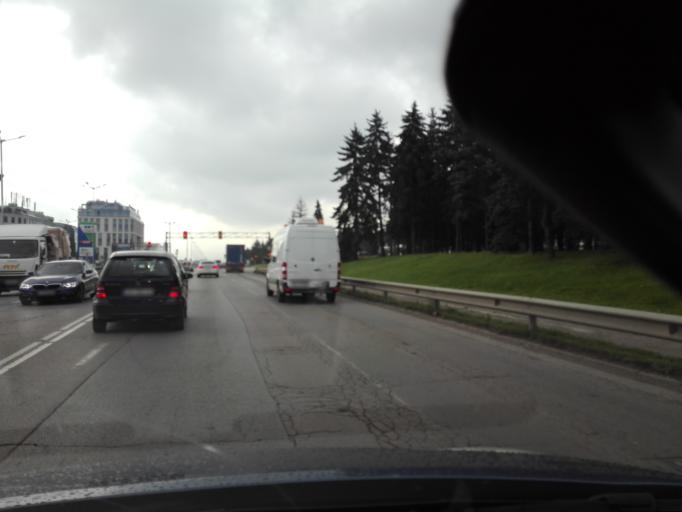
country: BG
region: Sofia-Capital
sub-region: Stolichna Obshtina
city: Sofia
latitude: 42.6580
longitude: 23.2707
